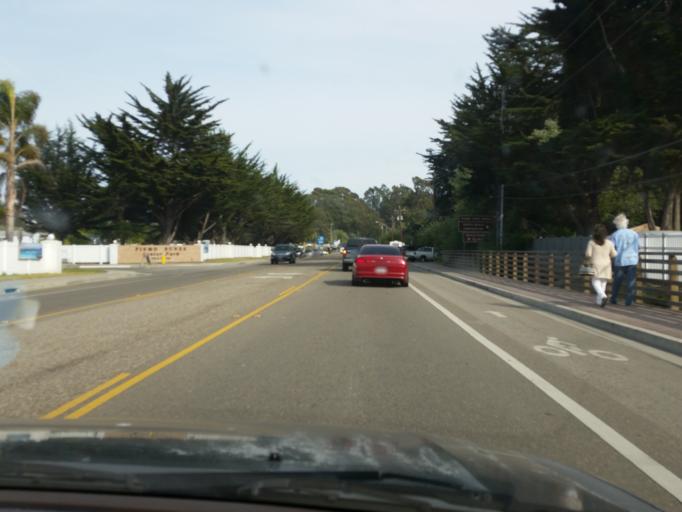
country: US
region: California
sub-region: San Luis Obispo County
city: Pismo Beach
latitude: 35.1338
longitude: -120.6355
